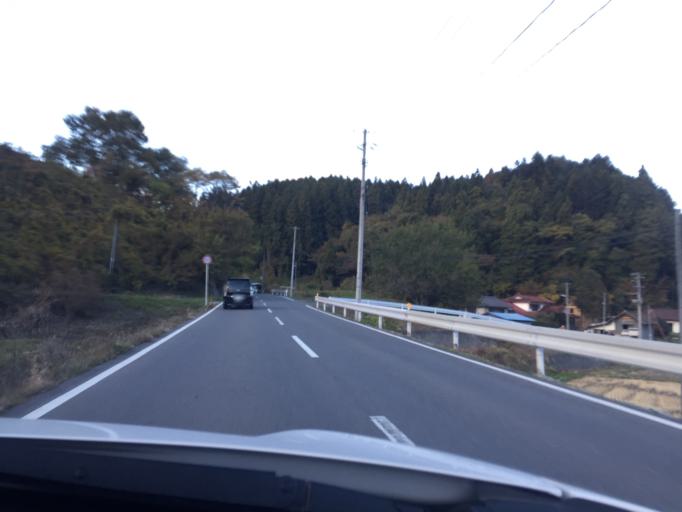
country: JP
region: Fukushima
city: Ishikawa
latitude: 37.2194
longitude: 140.6299
